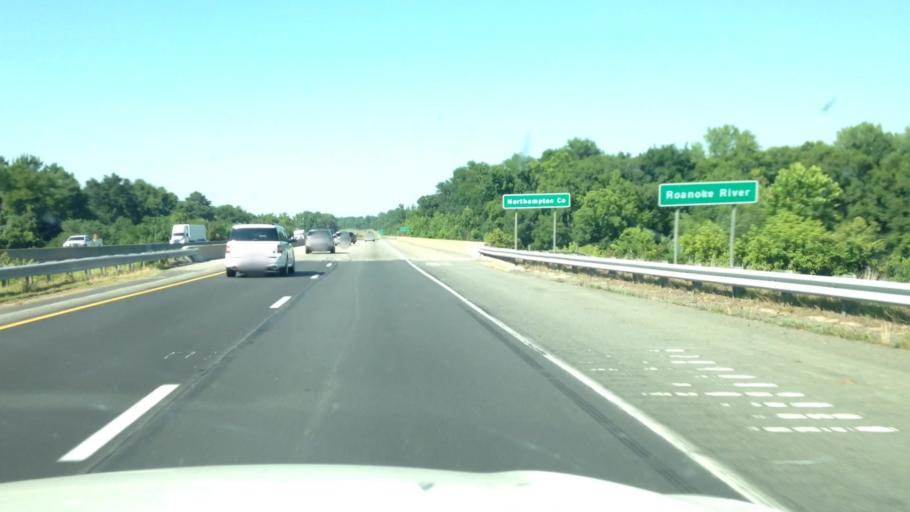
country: US
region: North Carolina
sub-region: Halifax County
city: Roanoke Rapids
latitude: 36.4443
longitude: -77.6255
